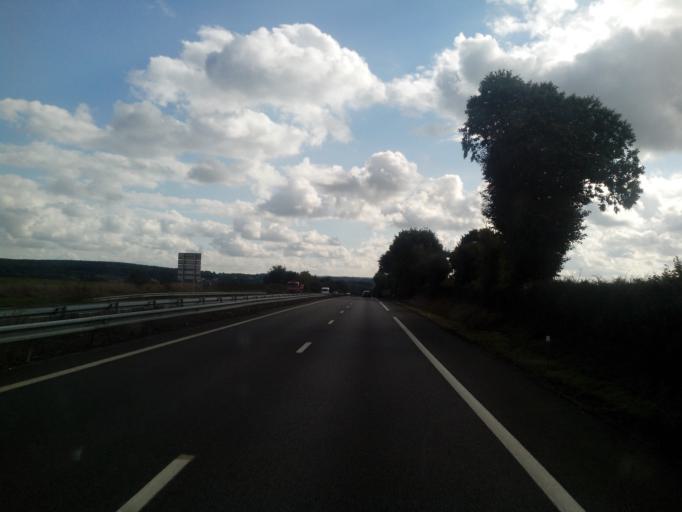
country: FR
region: Brittany
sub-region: Departement du Morbihan
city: Ploermel
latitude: 47.9053
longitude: -2.4104
